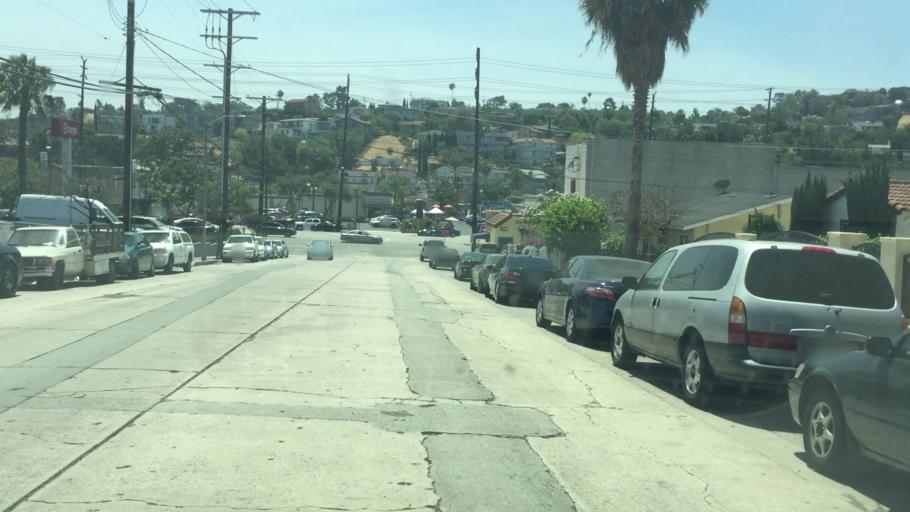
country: US
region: California
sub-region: Los Angeles County
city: Glendale
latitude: 34.1228
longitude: -118.2259
